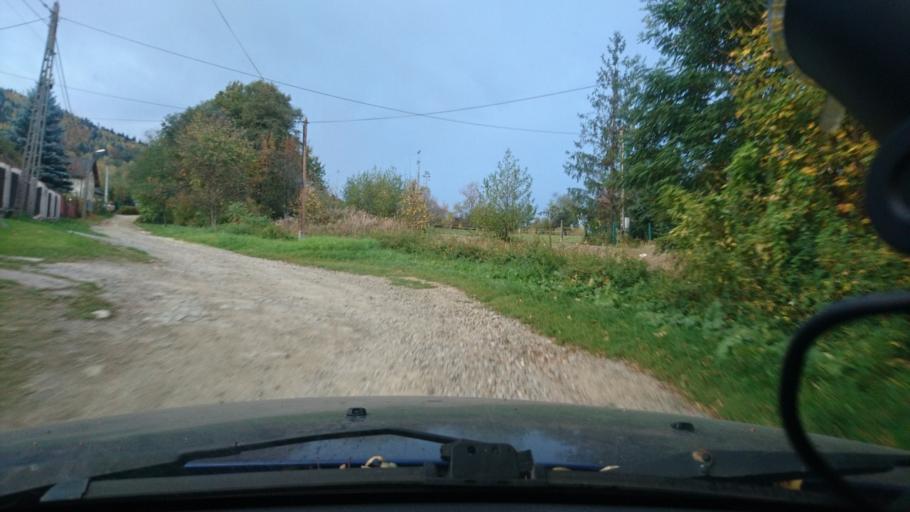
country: PL
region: Silesian Voivodeship
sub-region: Powiat bielski
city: Wilkowice
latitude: 49.7960
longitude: 19.0920
